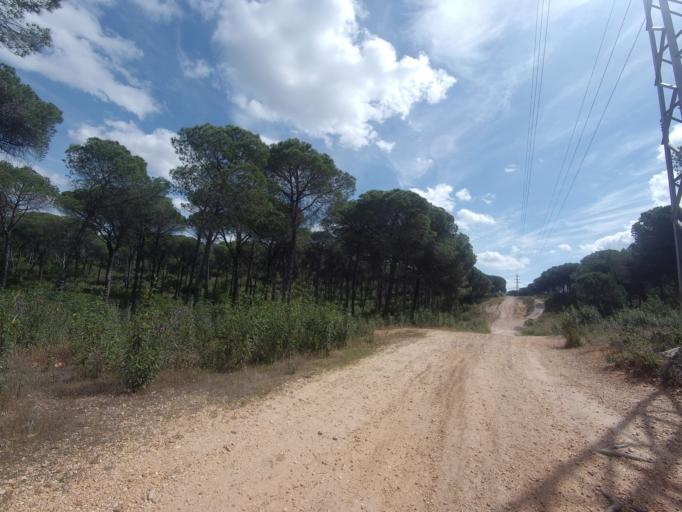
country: ES
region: Andalusia
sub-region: Provincia de Huelva
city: Aljaraque
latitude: 37.2246
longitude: -7.0678
